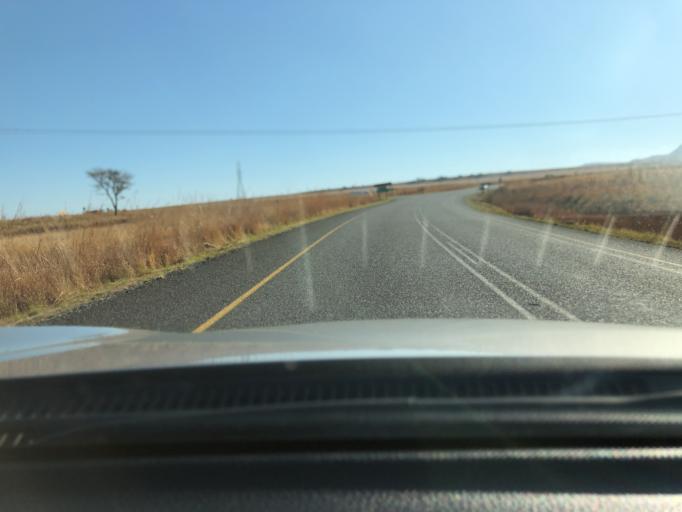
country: ZA
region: KwaZulu-Natal
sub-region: uThukela District Municipality
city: Ekuvukeni
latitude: -28.4065
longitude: 29.9548
